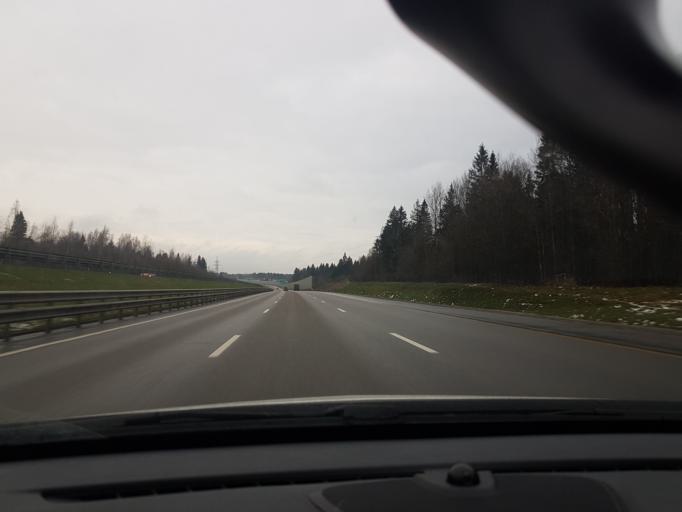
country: RU
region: Moskovskaya
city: Novopetrovskoye
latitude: 55.9690
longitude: 36.4932
